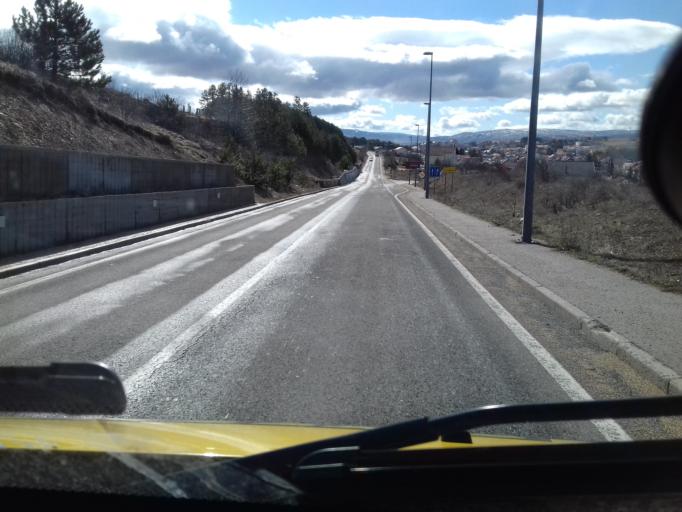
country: BA
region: Federation of Bosnia and Herzegovina
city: Tomislavgrad
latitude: 43.7299
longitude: 17.2226
